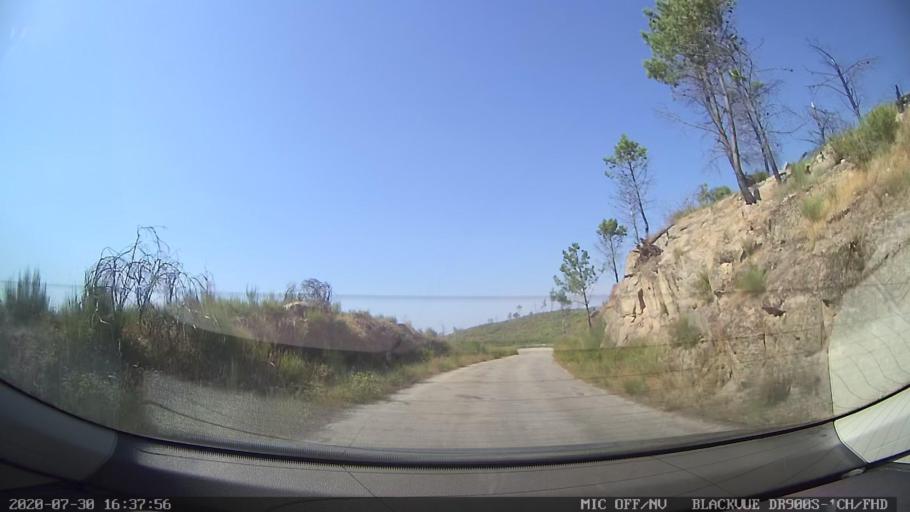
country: PT
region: Vila Real
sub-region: Sabrosa
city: Sabrosa
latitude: 41.3042
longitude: -7.4873
